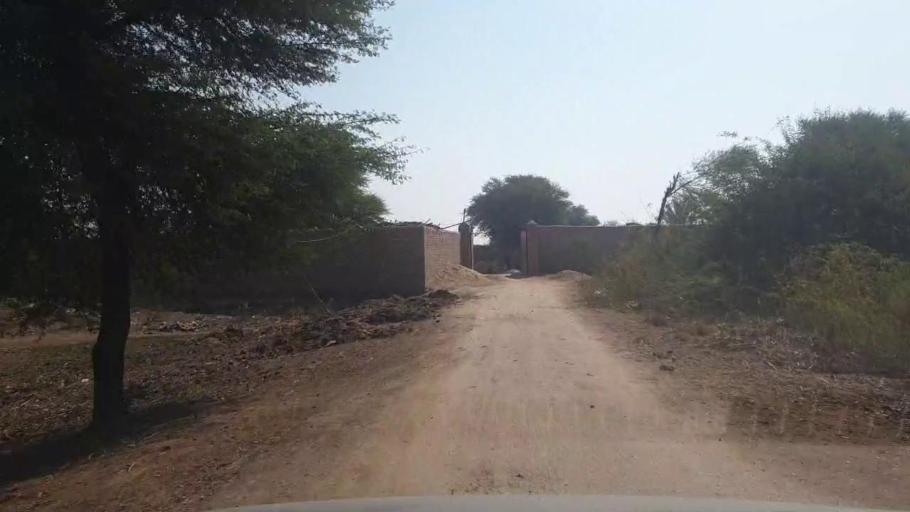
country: PK
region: Sindh
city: Chambar
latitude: 25.3605
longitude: 68.7806
